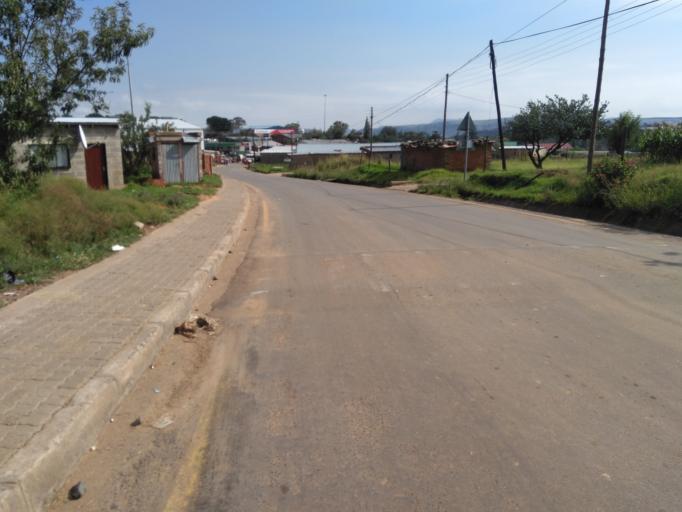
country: LS
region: Butha-Buthe
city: Butha-Buthe
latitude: -28.7704
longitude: 28.2502
